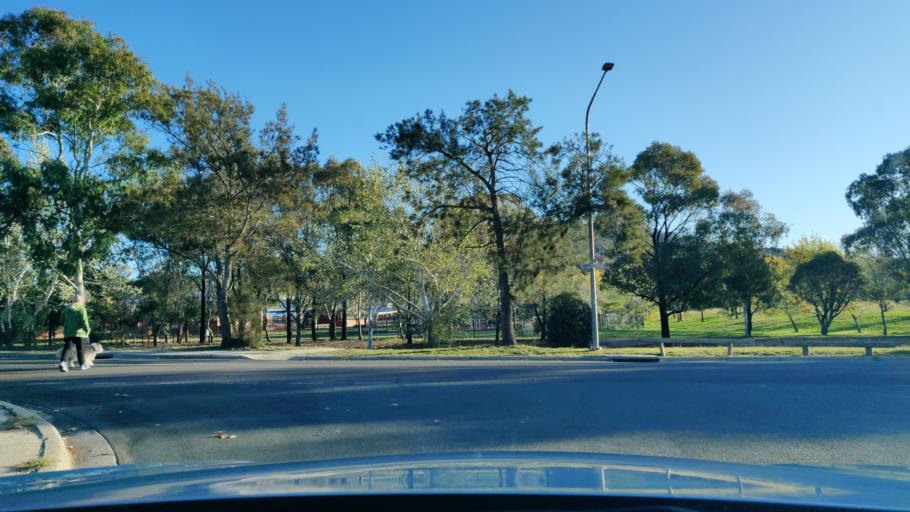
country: AU
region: Australian Capital Territory
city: Macarthur
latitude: -35.4460
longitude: 149.1243
